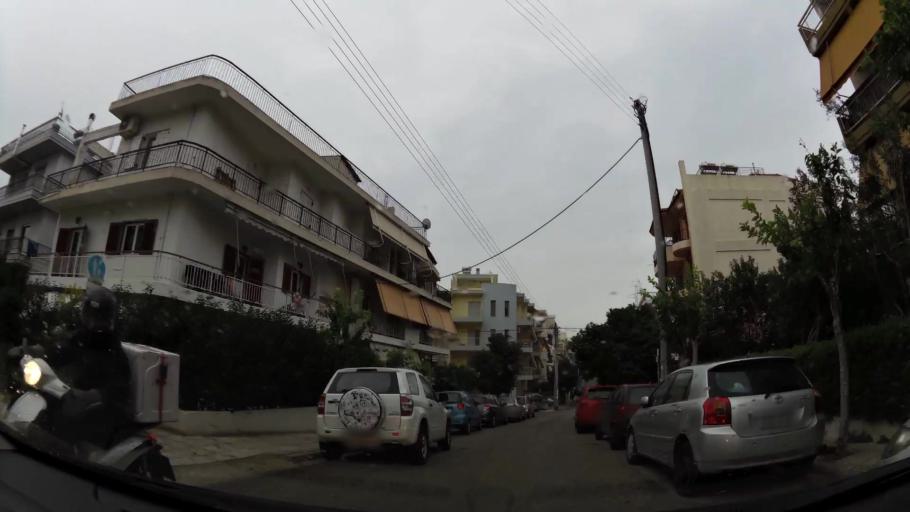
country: GR
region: Attica
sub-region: Nomarchia Athinas
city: Chaidari
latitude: 38.0081
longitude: 23.6622
